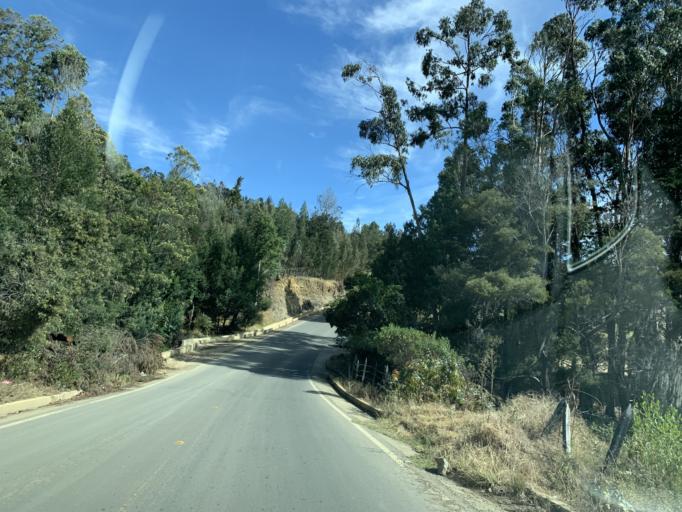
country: CO
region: Boyaca
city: Santa Sofia
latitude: 5.7121
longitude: -73.6057
